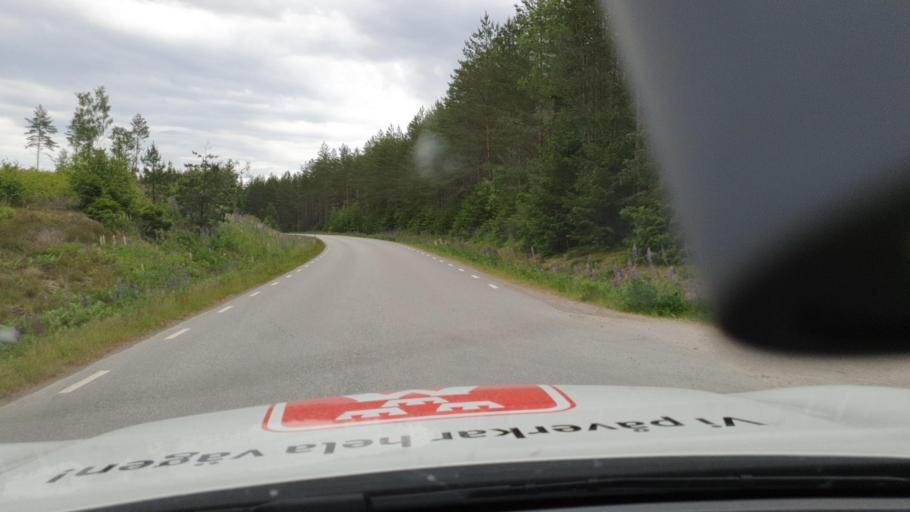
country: SE
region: Vaestra Goetaland
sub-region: Karlsborgs Kommun
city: Karlsborg
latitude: 58.6698
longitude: 14.4800
